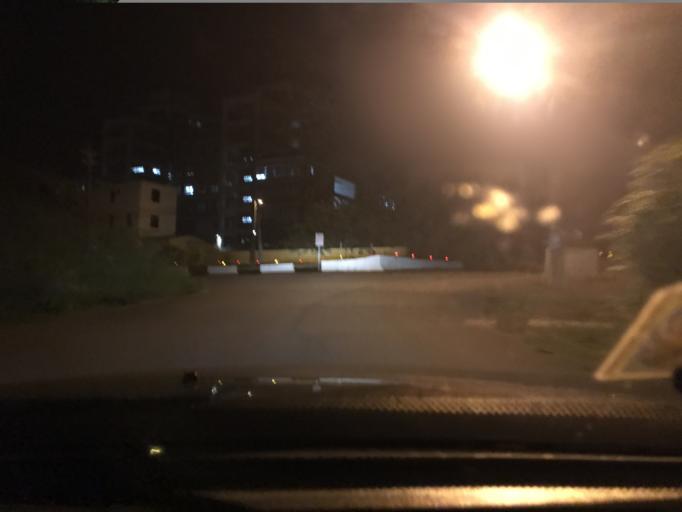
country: TW
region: Taiwan
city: Daxi
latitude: 24.9046
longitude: 121.2288
